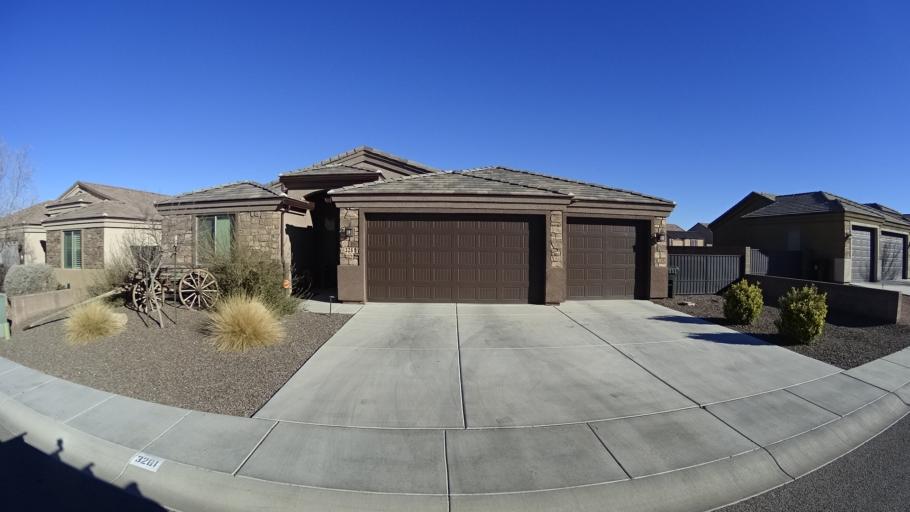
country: US
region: Arizona
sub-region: Mohave County
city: Kingman
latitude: 35.1871
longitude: -114.0006
